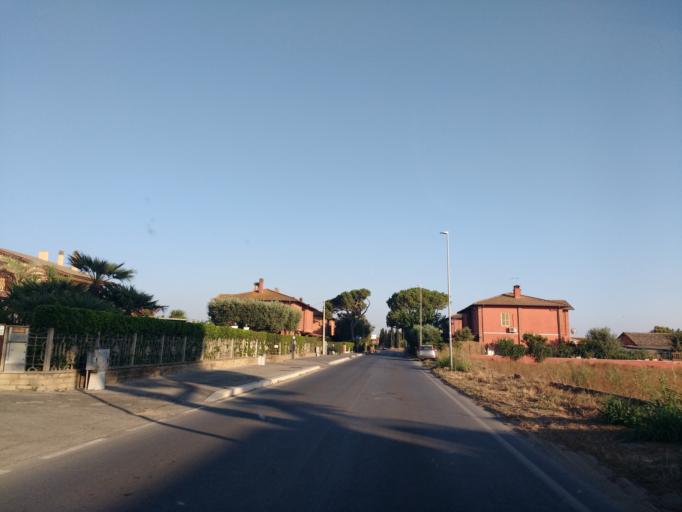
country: IT
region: Latium
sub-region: Citta metropolitana di Roma Capitale
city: Focene
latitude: 41.8368
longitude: 12.2291
